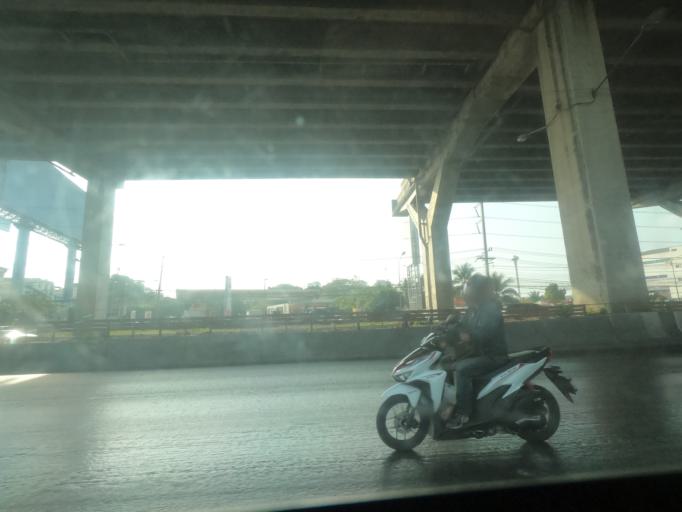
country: TH
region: Bangkok
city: Sai Mai
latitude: 13.9720
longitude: 100.6492
